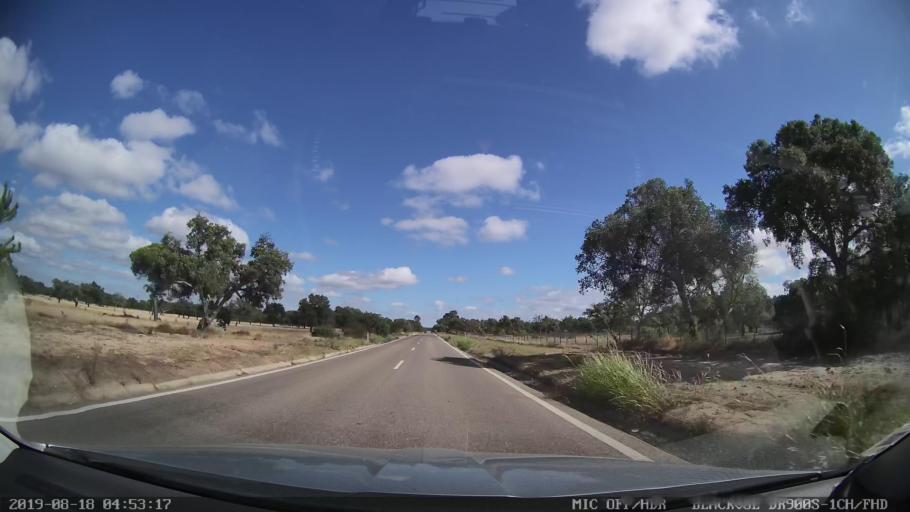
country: PT
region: Santarem
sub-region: Benavente
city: Poceirao
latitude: 38.9016
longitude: -8.7564
